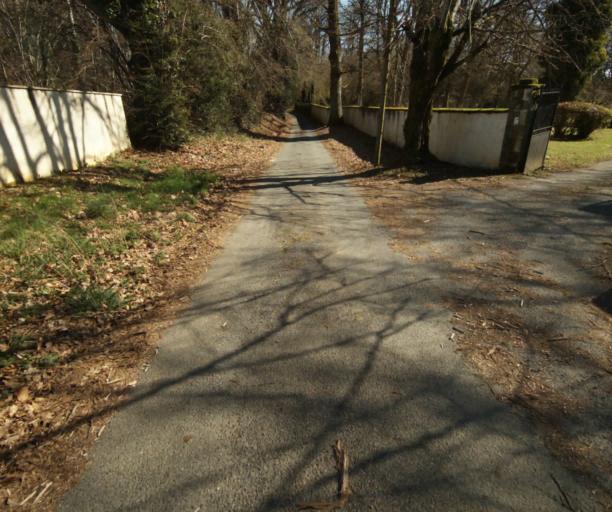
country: FR
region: Limousin
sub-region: Departement de la Correze
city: Chamboulive
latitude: 45.4661
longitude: 1.7462
